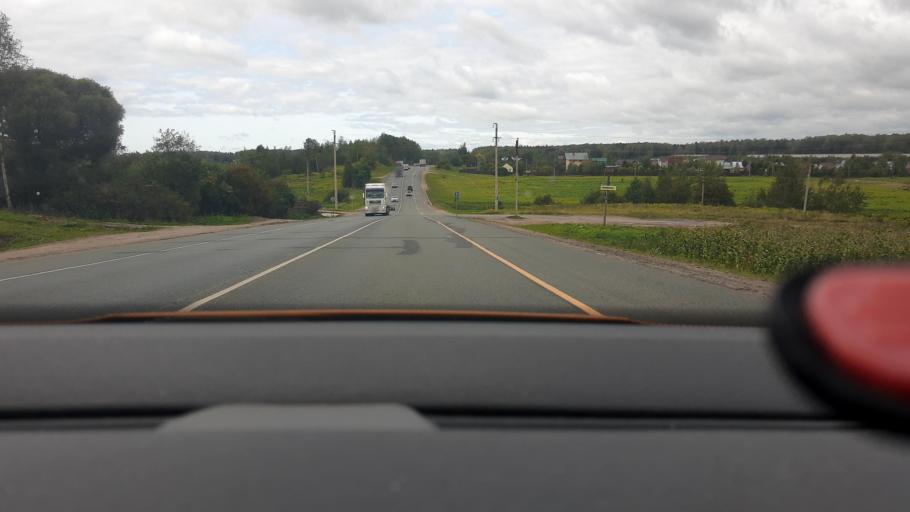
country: RU
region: Moskovskaya
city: Krasnoarmeysk
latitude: 56.0777
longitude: 38.0332
